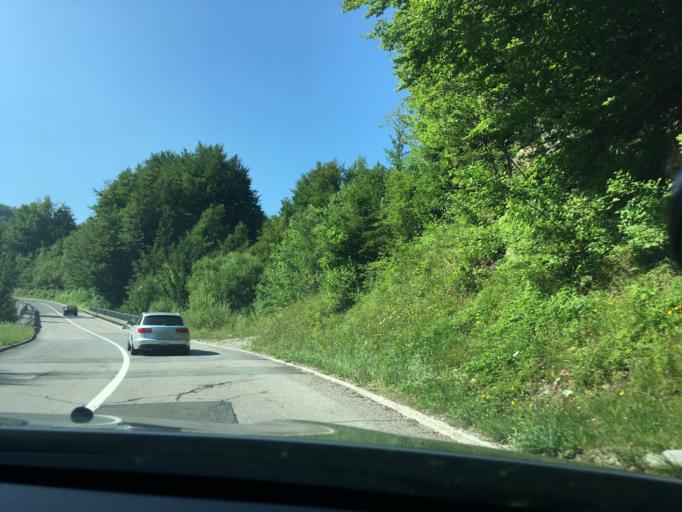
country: HR
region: Primorsko-Goranska
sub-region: Grad Delnice
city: Delnice
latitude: 45.4060
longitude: 14.8110
